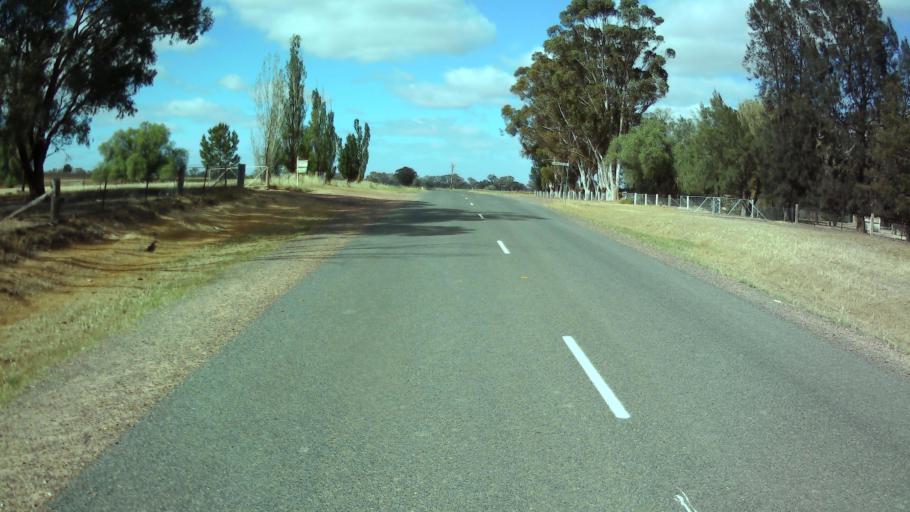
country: AU
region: New South Wales
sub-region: Weddin
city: Grenfell
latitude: -33.9563
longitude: 148.4376
